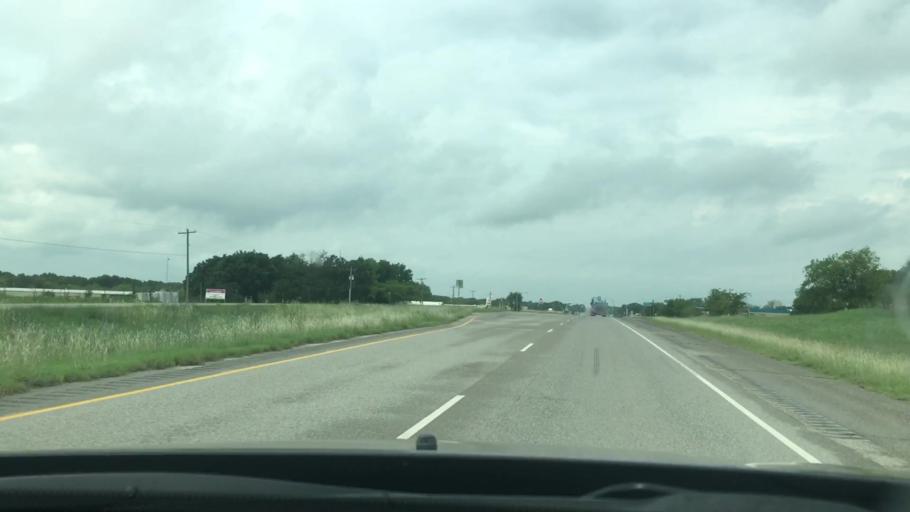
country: US
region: Oklahoma
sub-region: Carter County
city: Wilson
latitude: 34.1731
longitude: -97.4705
